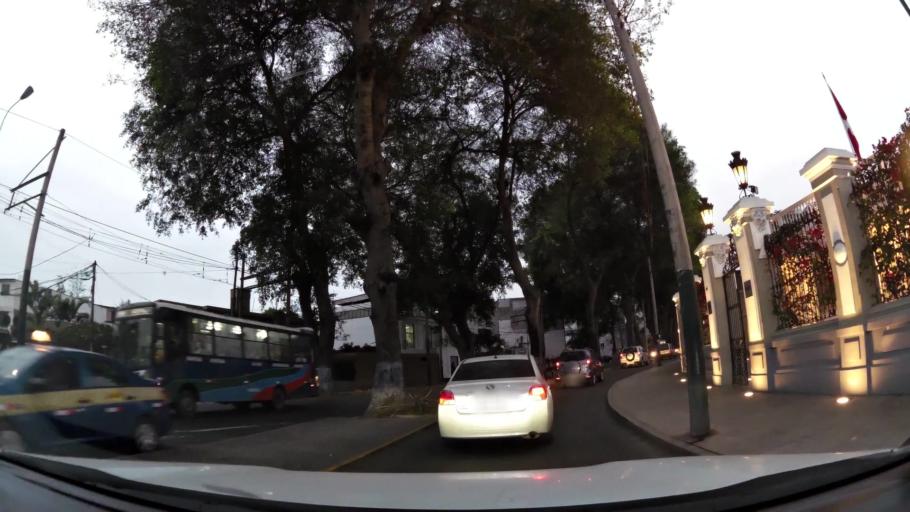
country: PE
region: Lima
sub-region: Lima
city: Surco
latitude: -12.1543
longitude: -77.0231
